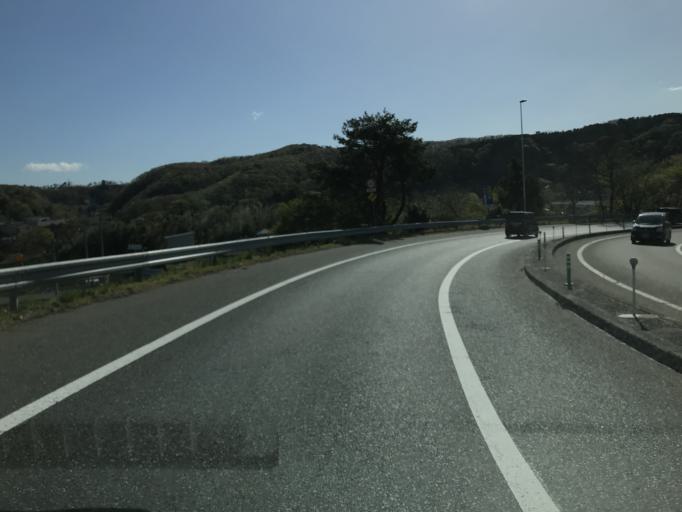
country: JP
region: Miyagi
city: Sendai
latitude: 38.2614
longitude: 140.8154
